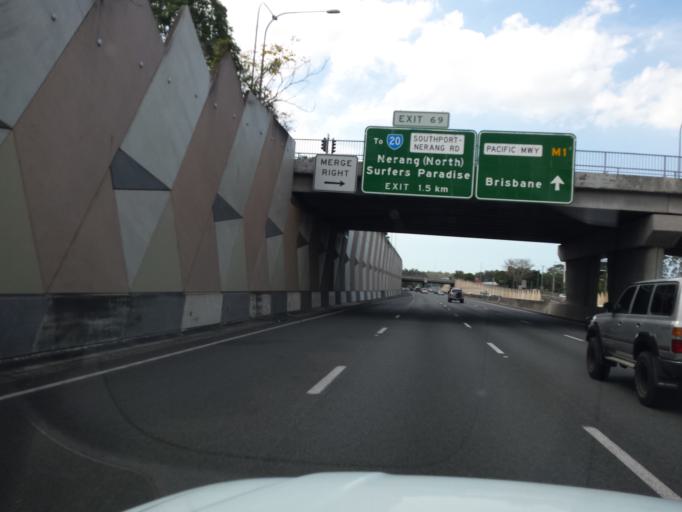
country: AU
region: Queensland
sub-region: Gold Coast
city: Nerang
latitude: -27.9971
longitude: 153.3398
